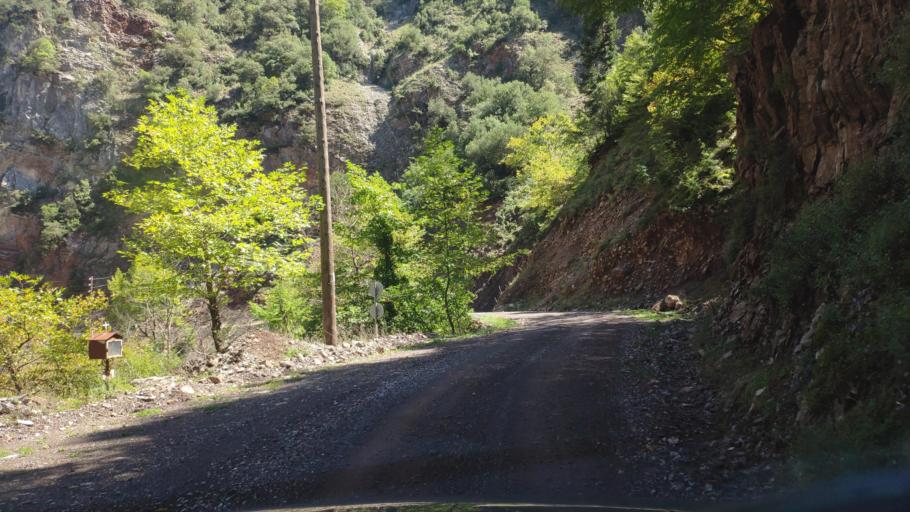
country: GR
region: Central Greece
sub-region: Nomos Evrytanias
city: Kerasochori
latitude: 39.1343
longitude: 21.6346
